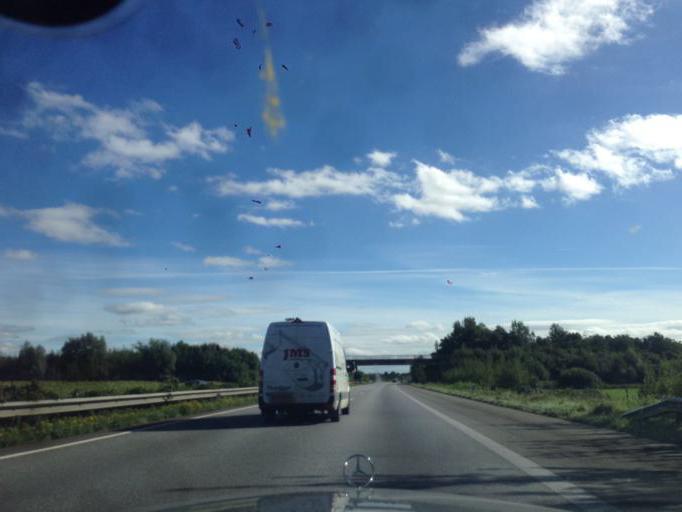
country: DE
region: Schleswig-Holstein
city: Bollingstedt
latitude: 54.5867
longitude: 9.4639
